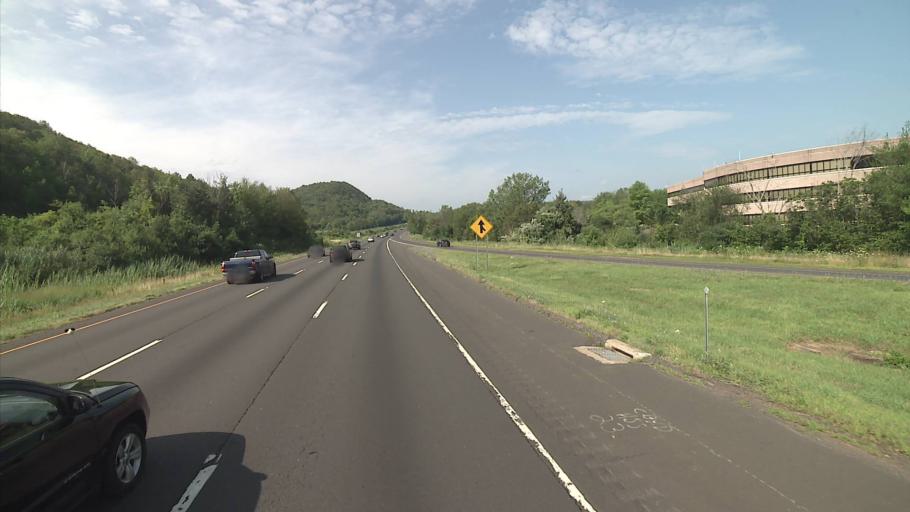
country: US
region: Connecticut
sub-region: Middlesex County
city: Middletown
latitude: 41.5691
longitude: -72.7263
